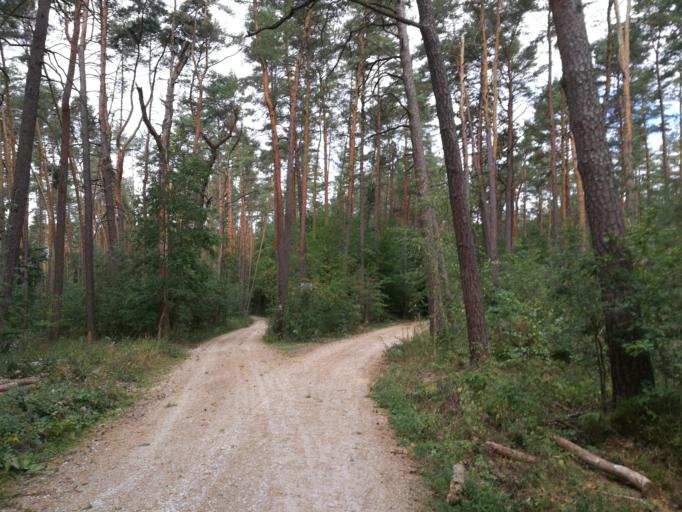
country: DE
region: Bavaria
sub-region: Regierungsbezirk Mittelfranken
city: Seukendorf
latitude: 49.4748
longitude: 10.9014
